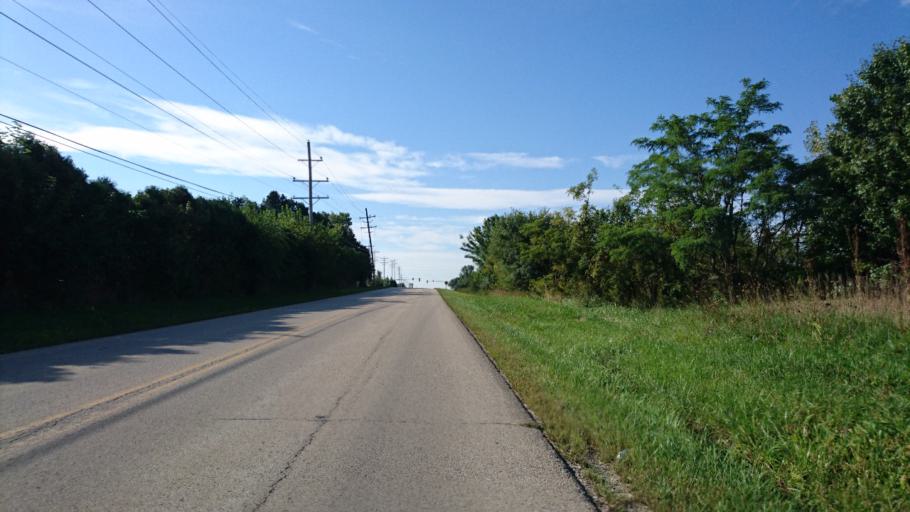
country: US
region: Illinois
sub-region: Will County
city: Ingalls Park
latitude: 41.4851
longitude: -88.0227
